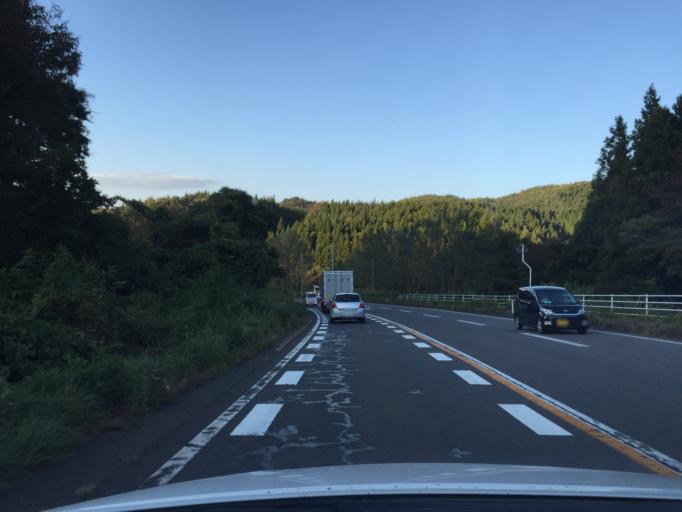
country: JP
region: Fukushima
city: Ishikawa
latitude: 37.2743
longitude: 140.5499
